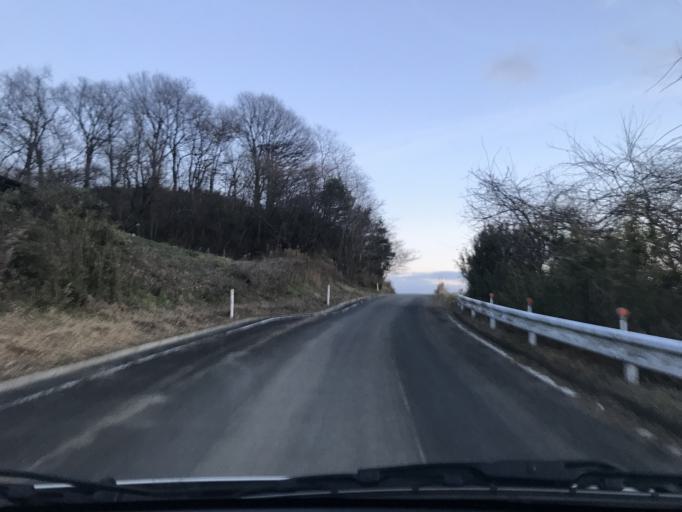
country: JP
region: Iwate
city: Ichinoseki
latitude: 38.8283
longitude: 141.0895
